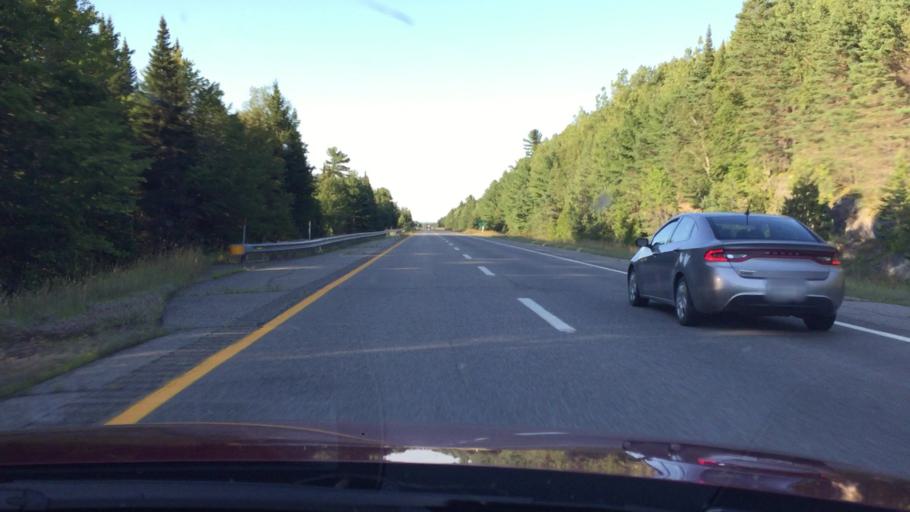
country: US
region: Maine
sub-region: Penobscot County
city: Patten
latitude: 45.8465
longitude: -68.4299
